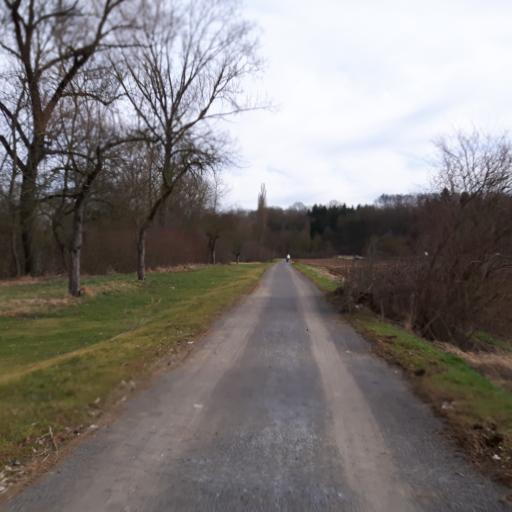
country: DE
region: Baden-Wuerttemberg
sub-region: Regierungsbezirk Stuttgart
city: Ilsfeld
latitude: 49.0531
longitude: 9.2243
